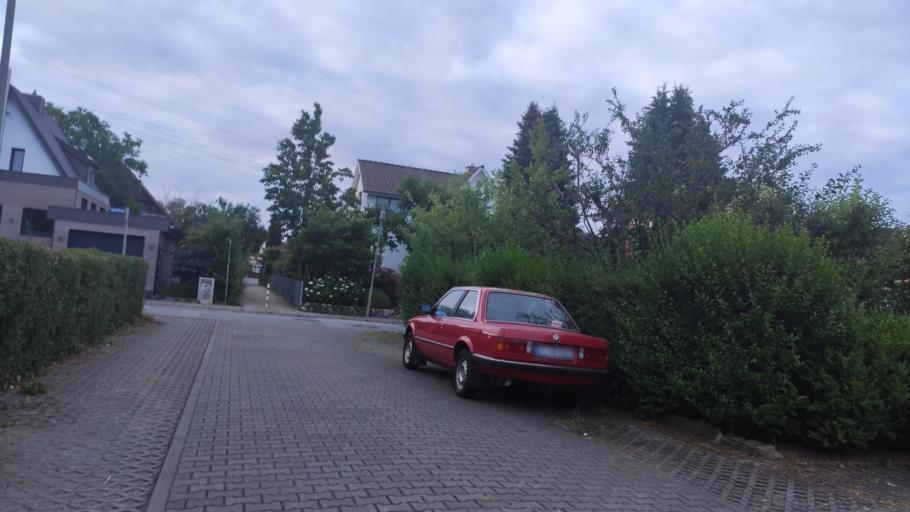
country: DE
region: Schleswig-Holstein
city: Geesthacht
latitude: 53.4418
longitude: 10.3559
